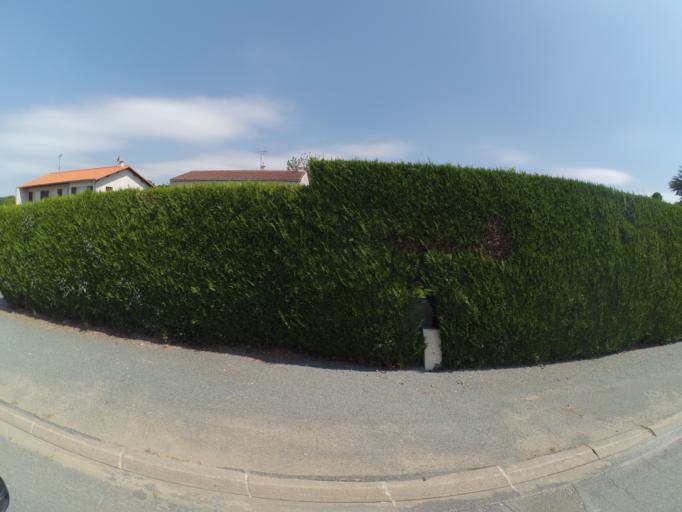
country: FR
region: Pays de la Loire
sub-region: Departement de la Vendee
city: Saint-Michel-Mont-Mercure
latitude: 46.8331
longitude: -0.8883
